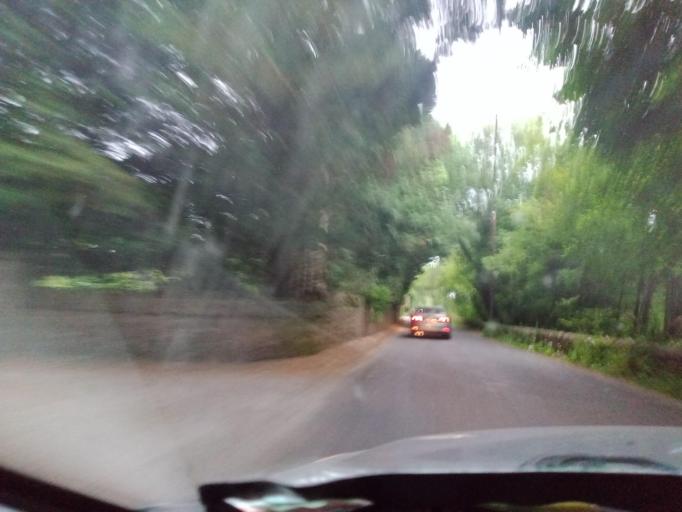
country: IE
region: Leinster
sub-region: Laois
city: Mountmellick
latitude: 53.1109
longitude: -7.3520
